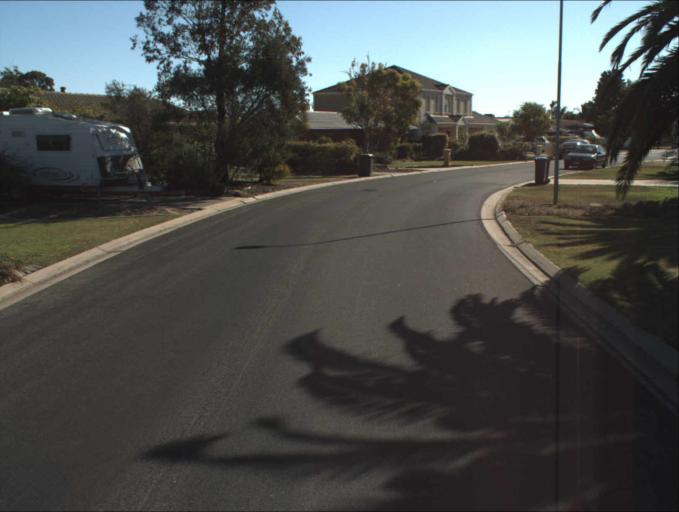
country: AU
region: South Australia
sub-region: Port Adelaide Enfield
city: Birkenhead
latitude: -34.7838
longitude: 138.4996
